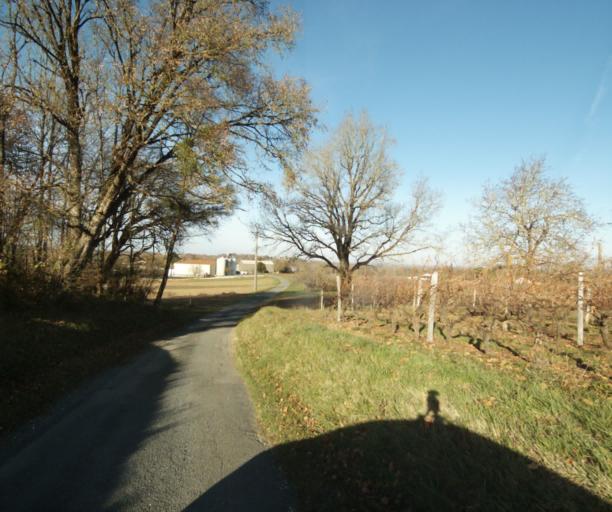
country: FR
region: Poitou-Charentes
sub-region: Departement de la Charente-Maritime
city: Burie
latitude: 45.7817
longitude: -0.4345
